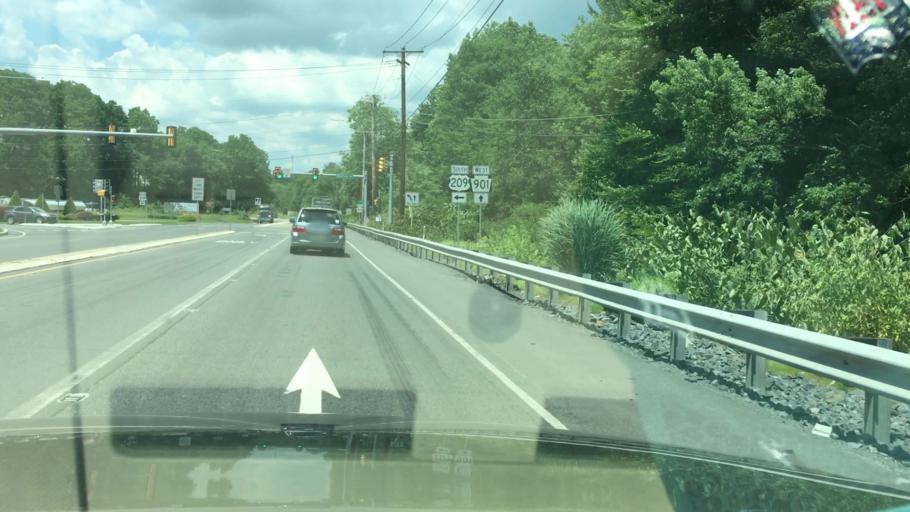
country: US
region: Pennsylvania
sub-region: Schuylkill County
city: Minersville
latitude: 40.6781
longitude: -76.2474
